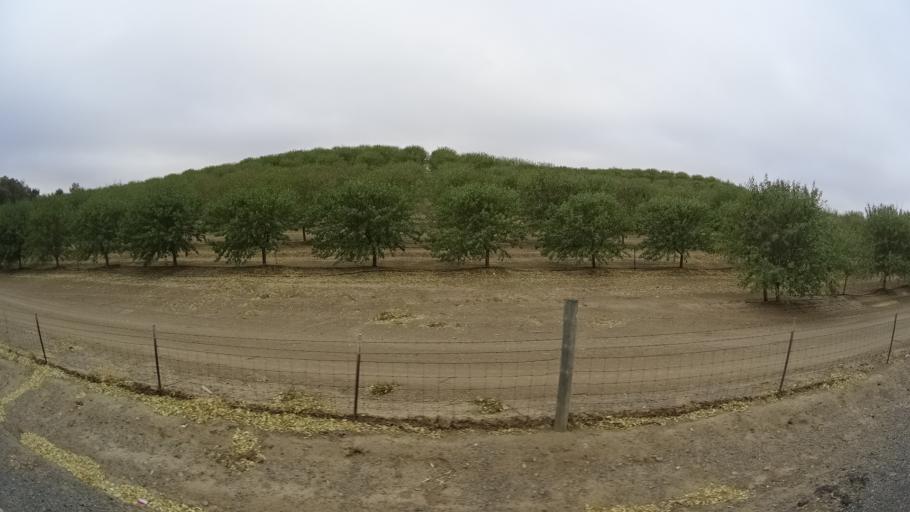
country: US
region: California
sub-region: Yolo County
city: Dunnigan
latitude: 38.8722
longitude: -122.0265
